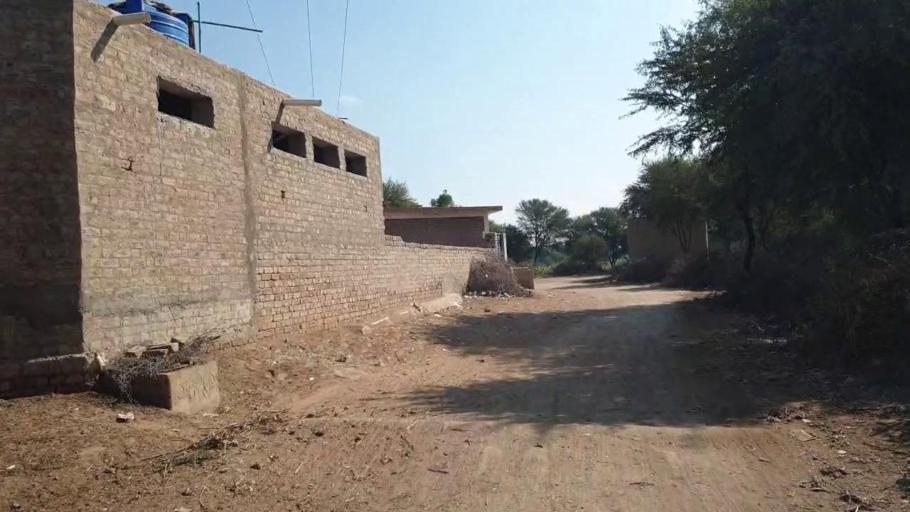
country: PK
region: Sindh
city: Shahpur Chakar
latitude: 26.0547
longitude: 68.5992
